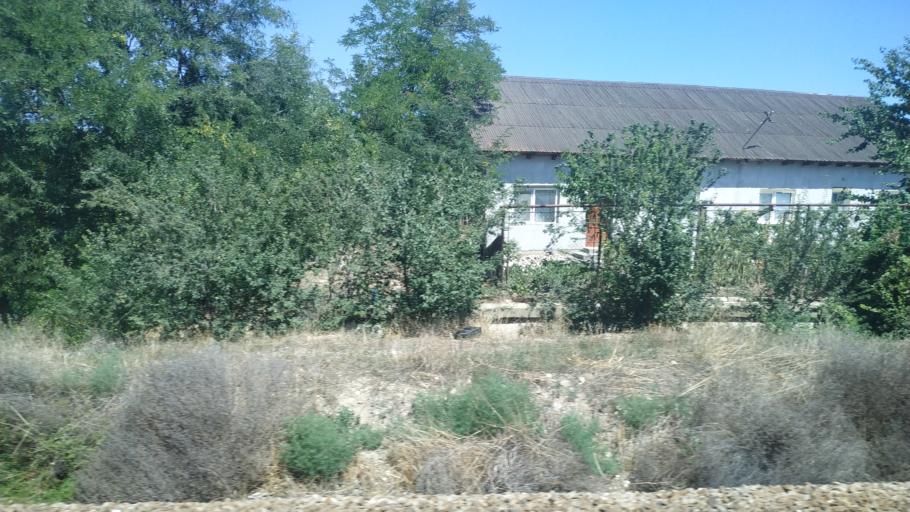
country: RO
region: Constanta
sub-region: Oras Murfatlar
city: Murfatlar
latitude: 44.1731
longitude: 28.4079
